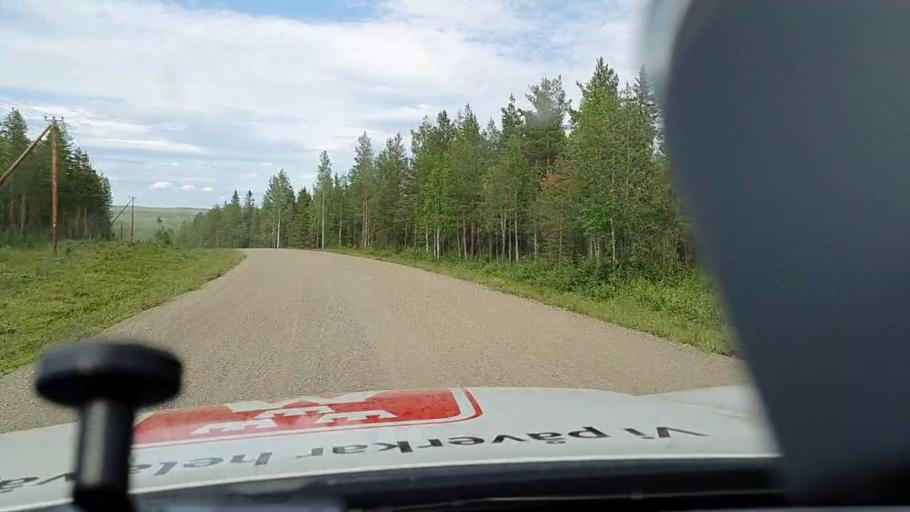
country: SE
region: Norrbotten
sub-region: Alvsbyns Kommun
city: AElvsbyn
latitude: 66.1419
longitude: 21.0162
